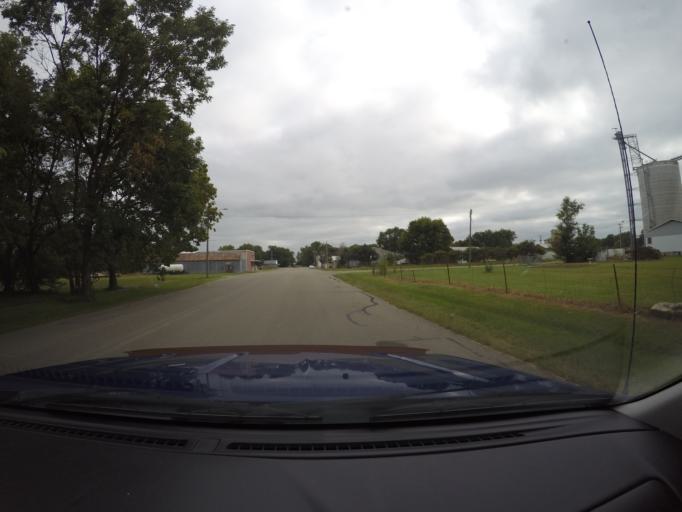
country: US
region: Kansas
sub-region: Dickinson County
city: Herington
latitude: 38.7972
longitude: -96.9573
